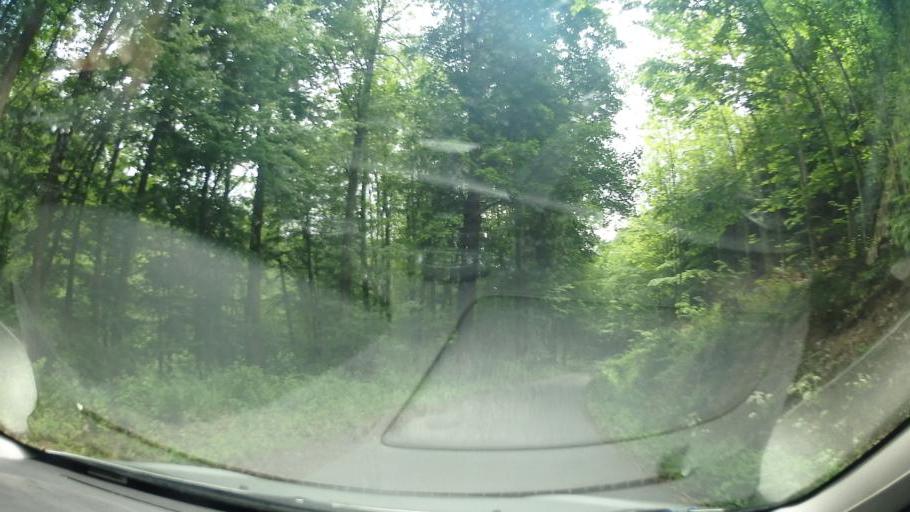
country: CZ
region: Olomoucky
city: Stity
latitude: 49.8670
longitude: 16.7403
